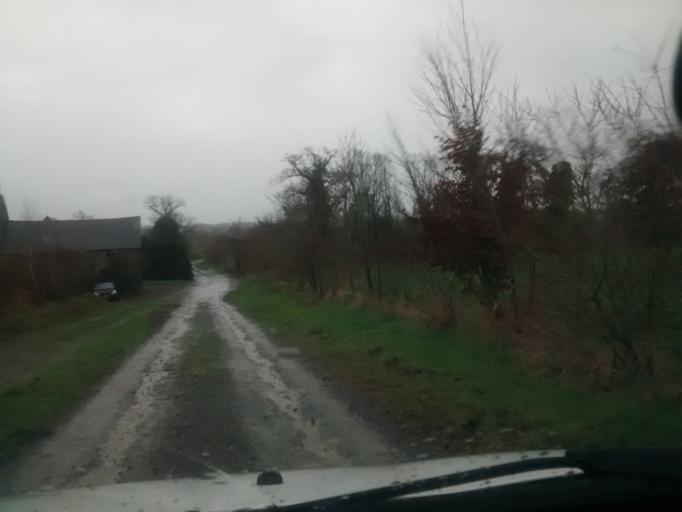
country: FR
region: Brittany
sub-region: Departement d'Ille-et-Vilaine
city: Saint-Pere
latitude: 48.5671
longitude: -1.9121
